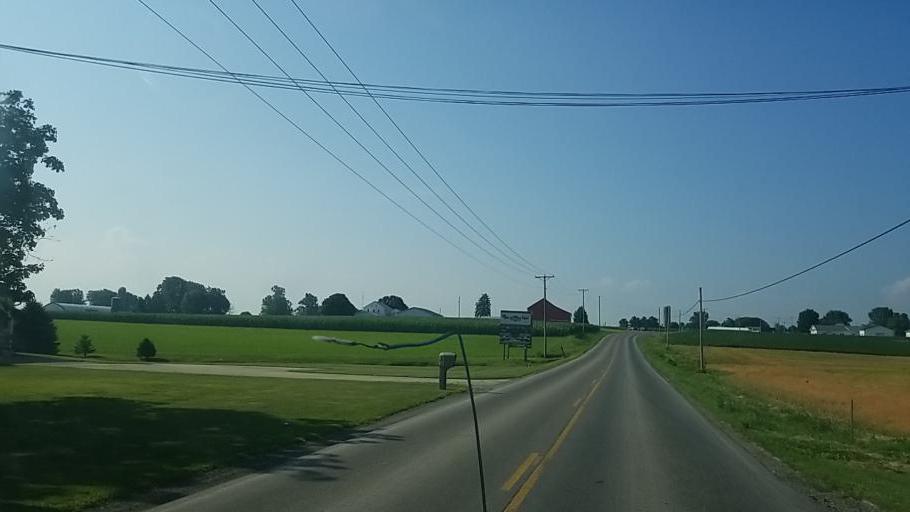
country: US
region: Ohio
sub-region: Wayne County
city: Dalton
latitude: 40.7255
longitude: -81.7450
